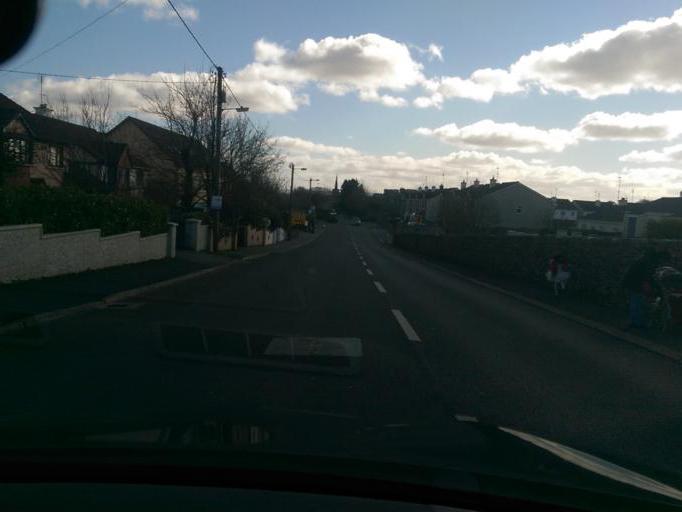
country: IE
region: Connaught
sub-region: County Galway
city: Athenry
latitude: 53.3042
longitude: -8.7501
